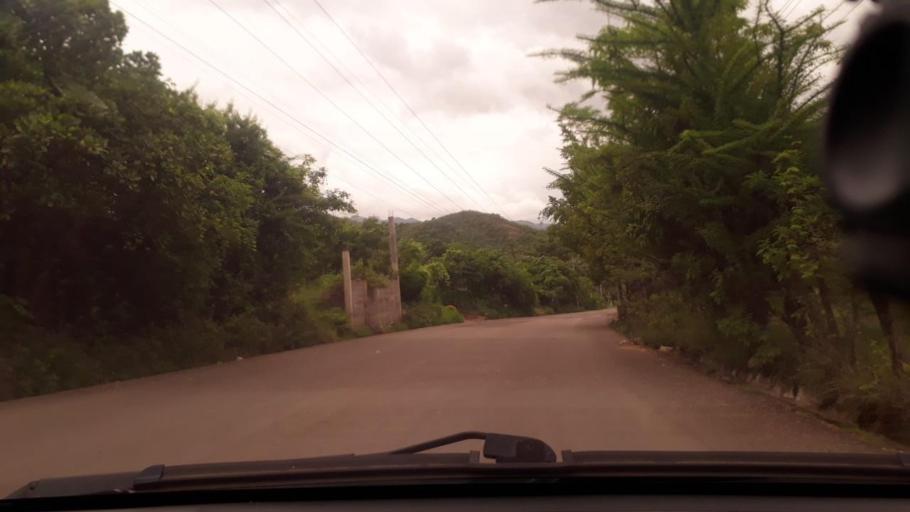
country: GT
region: Chiquimula
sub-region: Municipio de Jocotan
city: Jocotan
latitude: 14.8021
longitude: -89.3935
